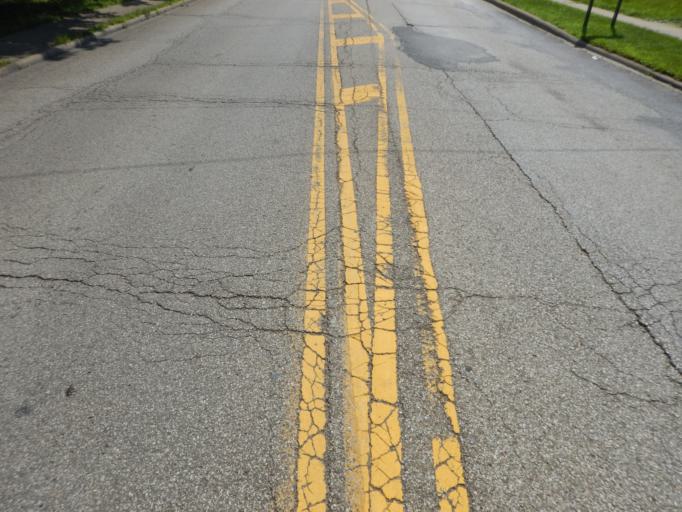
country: US
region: Ohio
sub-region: Muskingum County
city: Zanesville
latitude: 39.9535
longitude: -82.0183
